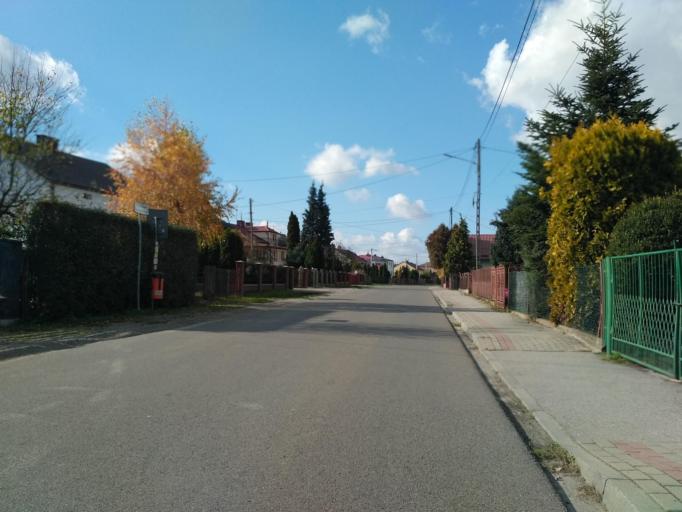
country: PL
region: Subcarpathian Voivodeship
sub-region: Powiat rzeszowski
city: Swilcza
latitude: 50.1146
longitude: 21.8702
